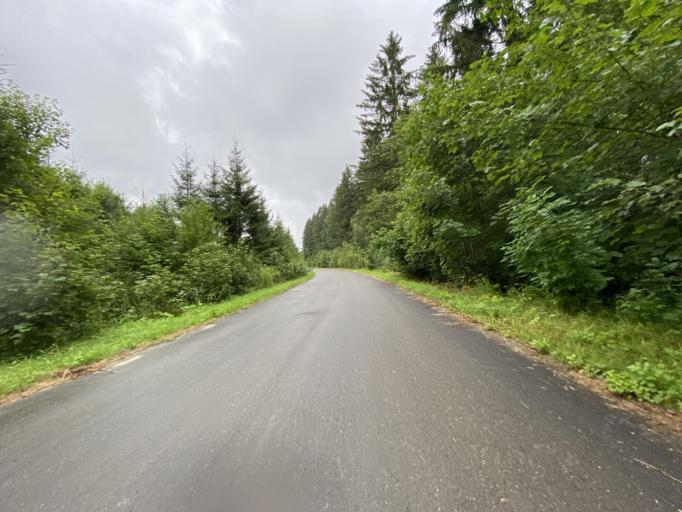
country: DE
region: Baden-Wuerttemberg
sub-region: Tuebingen Region
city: Sigmaringen
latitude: 48.1136
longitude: 9.2425
